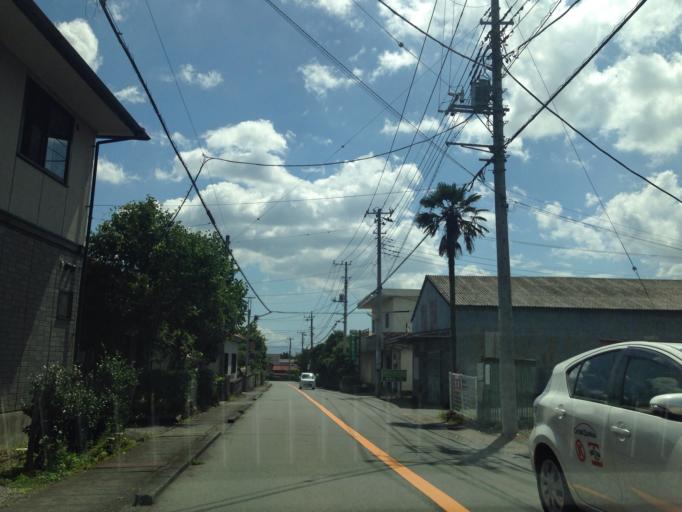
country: JP
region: Shizuoka
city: Mishima
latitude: 35.1951
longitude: 138.9080
